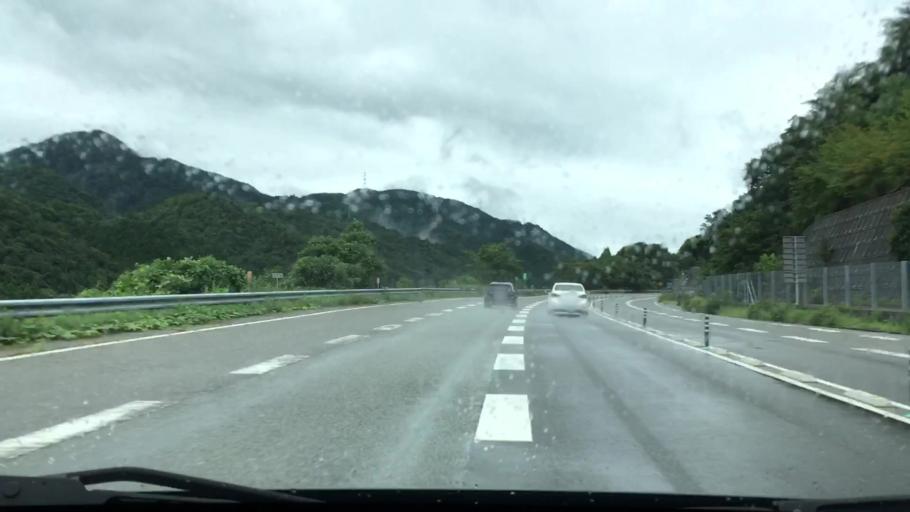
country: JP
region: Hyogo
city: Nishiwaki
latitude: 35.2105
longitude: 134.7943
